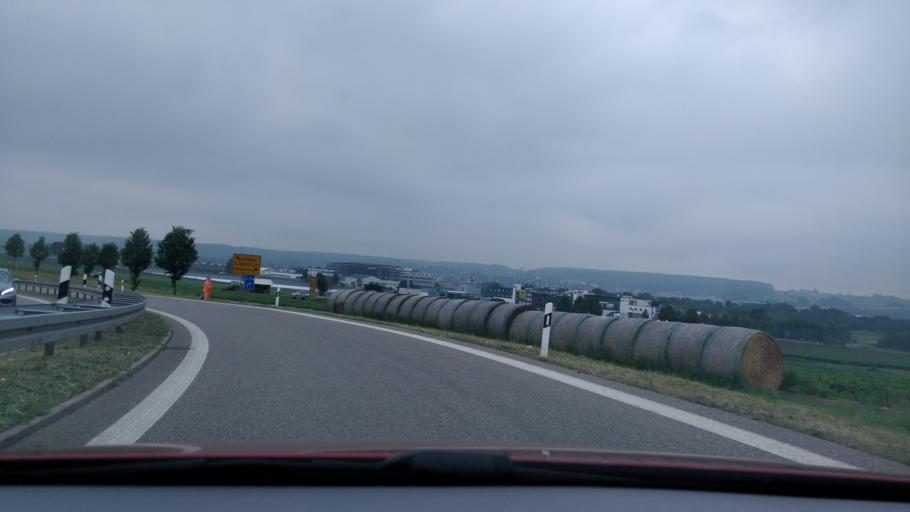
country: DE
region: Baden-Wuerttemberg
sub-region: Regierungsbezirk Stuttgart
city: Neuhausen auf den Fildern
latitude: 48.6945
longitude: 9.2628
